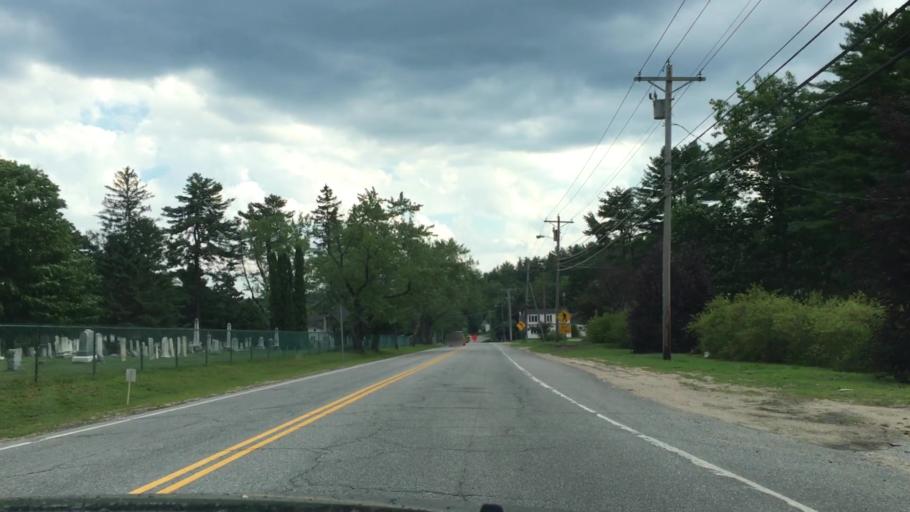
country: US
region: New Hampshire
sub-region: Belknap County
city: Meredith
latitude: 43.6687
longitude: -71.5028
